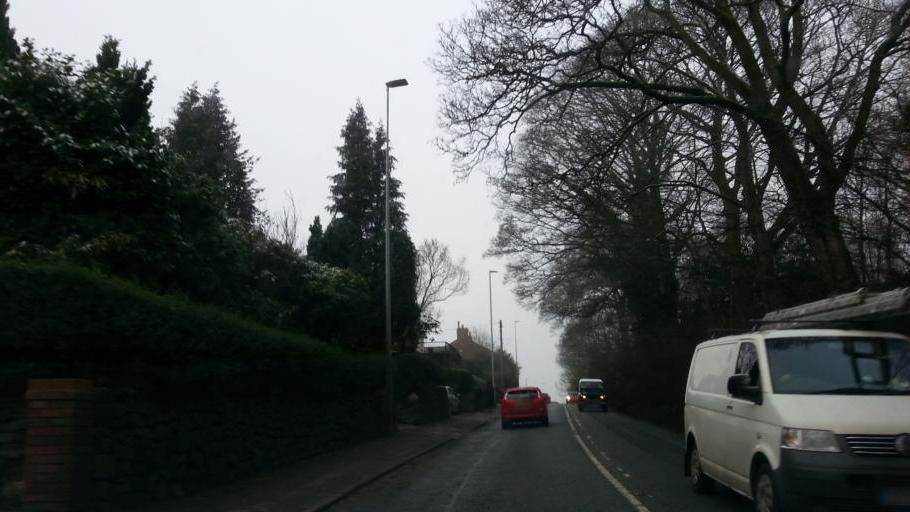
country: GB
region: England
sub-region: Staffordshire
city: Biddulph
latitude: 53.1489
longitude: -2.1783
